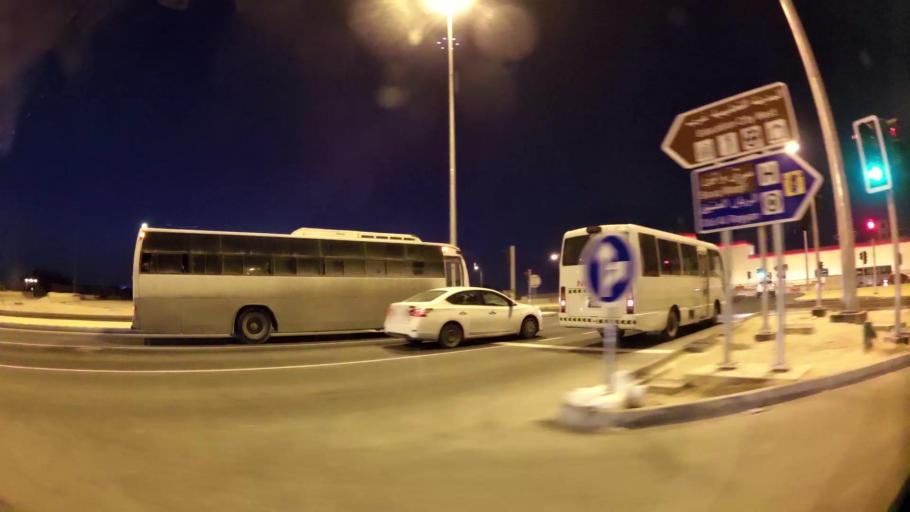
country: QA
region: Baladiyat ar Rayyan
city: Ar Rayyan
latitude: 25.3000
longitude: 51.4303
